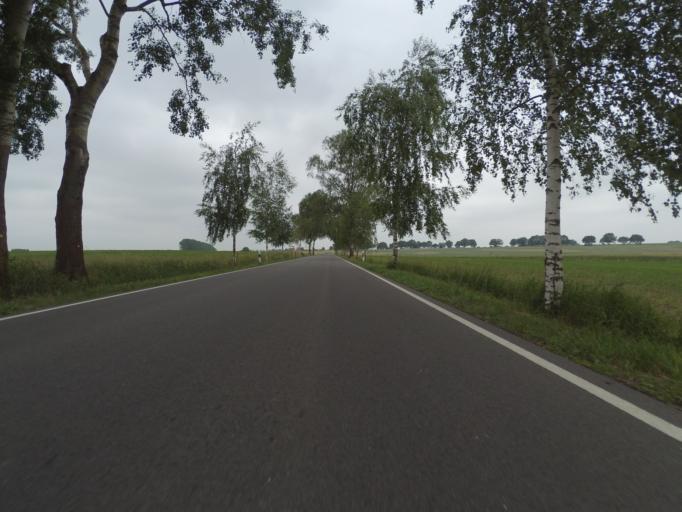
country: DE
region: Mecklenburg-Vorpommern
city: Domsuhl
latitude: 53.4872
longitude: 11.7156
